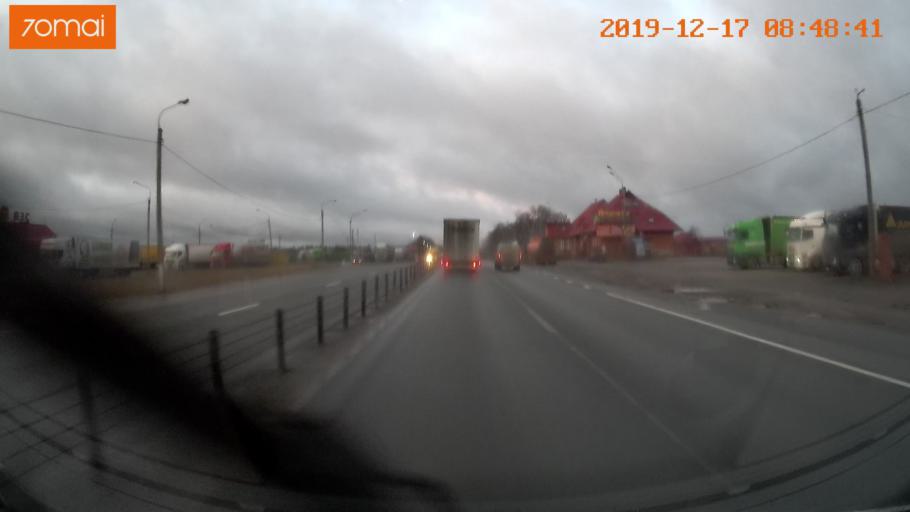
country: RU
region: Vladimir
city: Kosterevo
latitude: 55.9565
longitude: 39.6107
